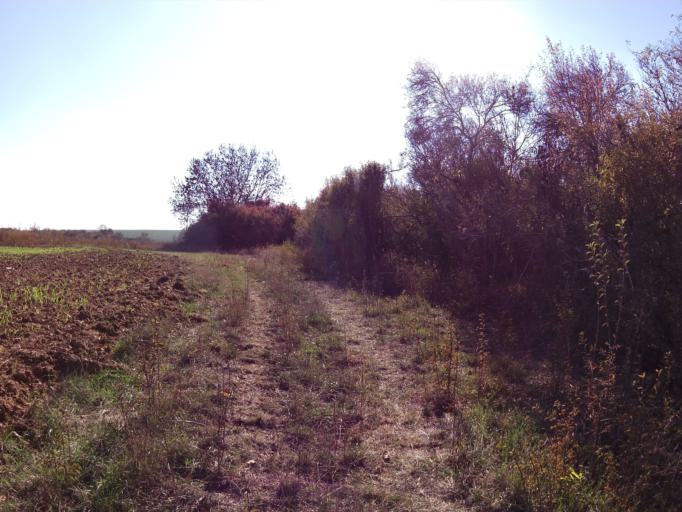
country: DE
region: Bavaria
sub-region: Regierungsbezirk Unterfranken
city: Eibelstadt
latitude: 49.7148
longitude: 9.9843
